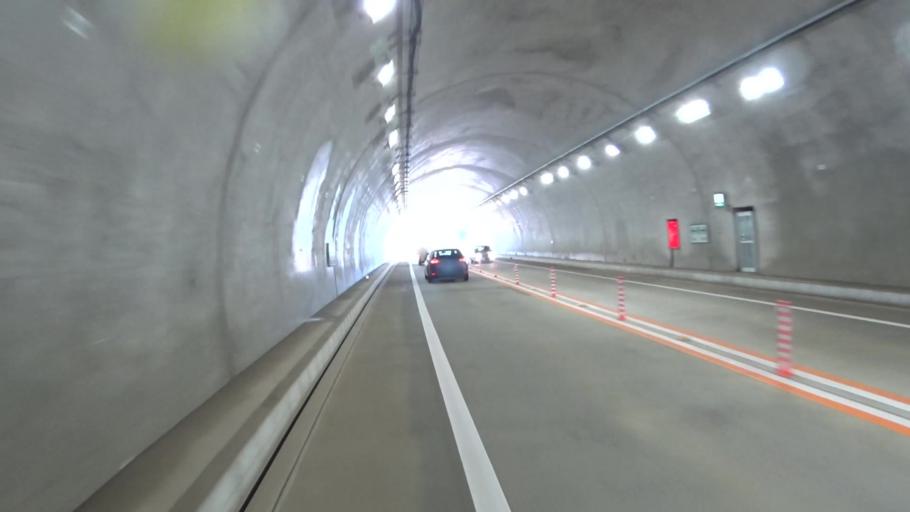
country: JP
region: Kyoto
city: Ayabe
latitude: 35.2093
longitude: 135.3462
